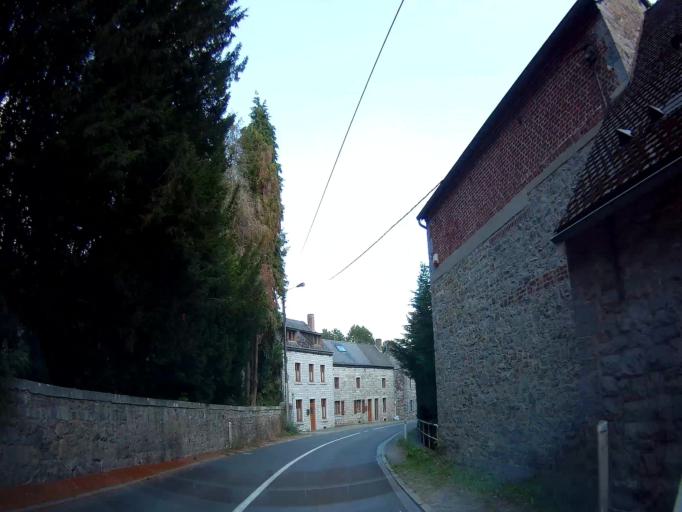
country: BE
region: Wallonia
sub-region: Province de Namur
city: Profondeville
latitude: 50.3472
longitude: 4.8465
